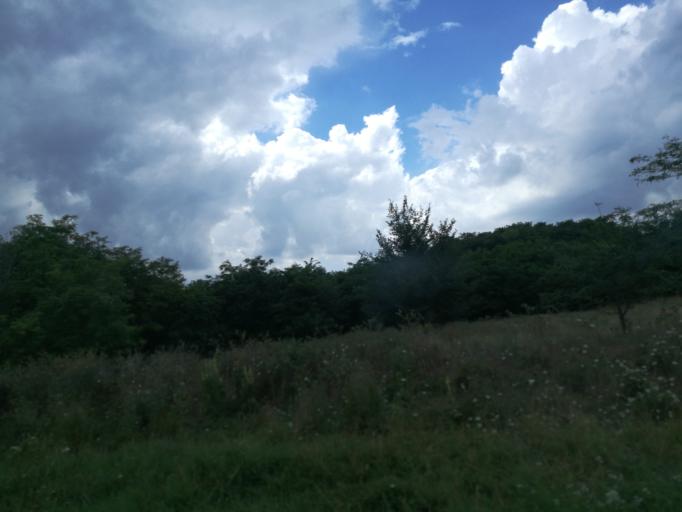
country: RO
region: Constanta
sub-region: Comuna Sacele
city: Sacele
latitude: 44.4442
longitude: 28.7319
